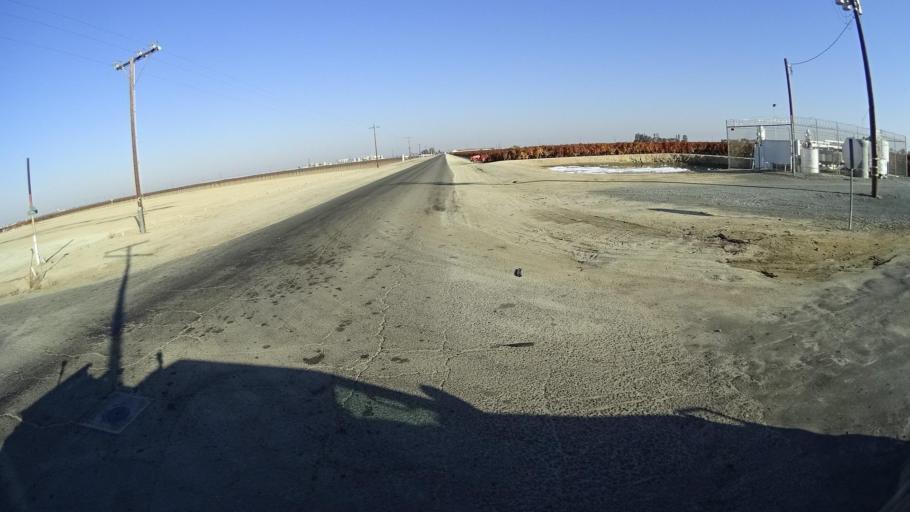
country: US
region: California
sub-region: Kern County
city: Delano
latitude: 35.7689
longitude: -119.1868
